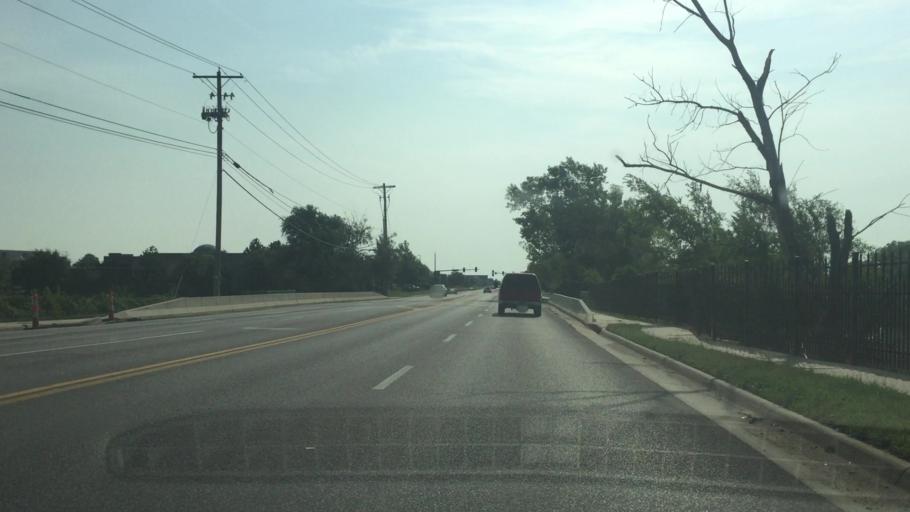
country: US
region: Kansas
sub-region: Sedgwick County
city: Bellaire
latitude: 37.7084
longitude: -97.2257
